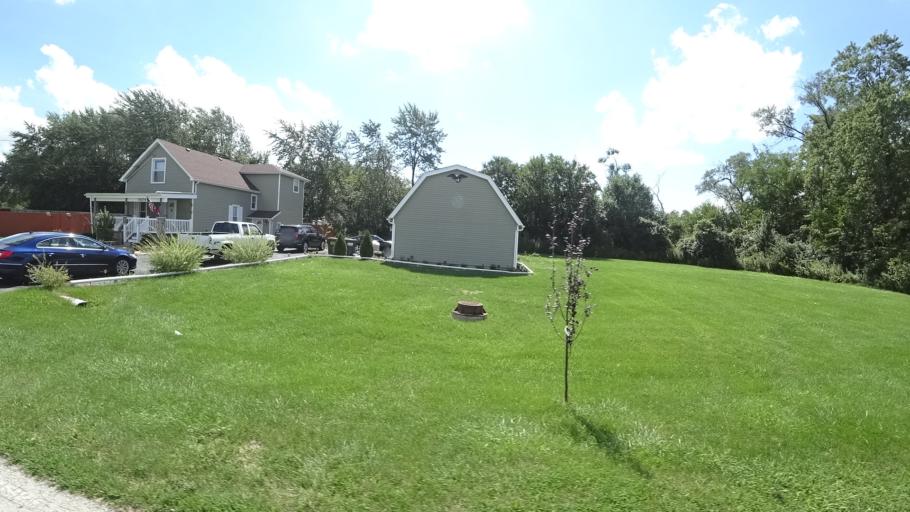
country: US
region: Illinois
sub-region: Cook County
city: Tinley Park
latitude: 41.5659
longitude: -87.7919
